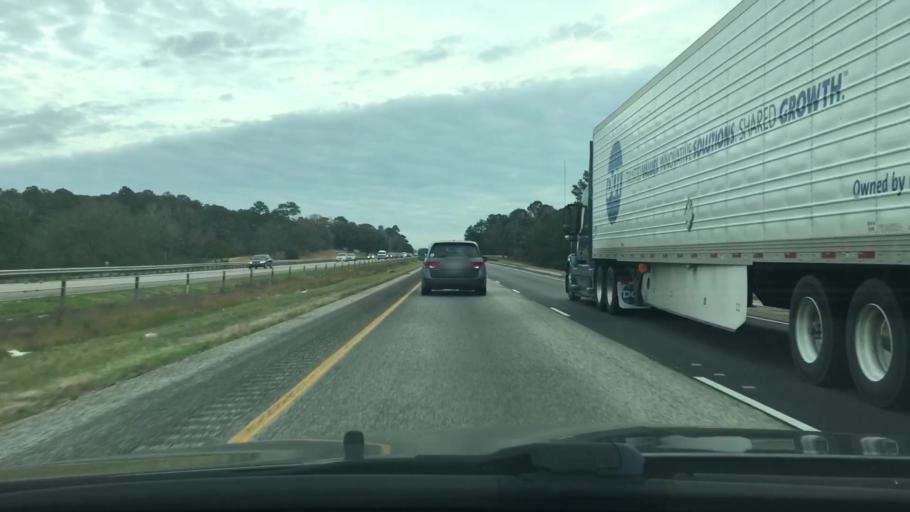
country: US
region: Texas
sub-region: Walker County
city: Huntsville
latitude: 30.8228
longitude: -95.7049
